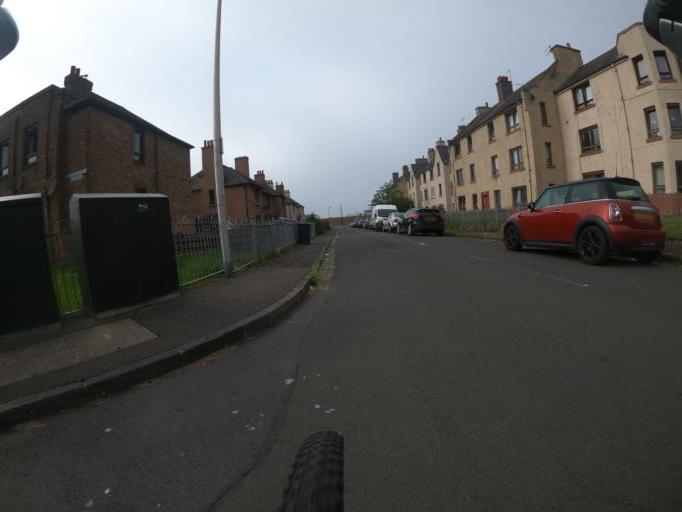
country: GB
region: Scotland
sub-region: Edinburgh
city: Edinburgh
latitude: 55.9772
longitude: -3.2341
